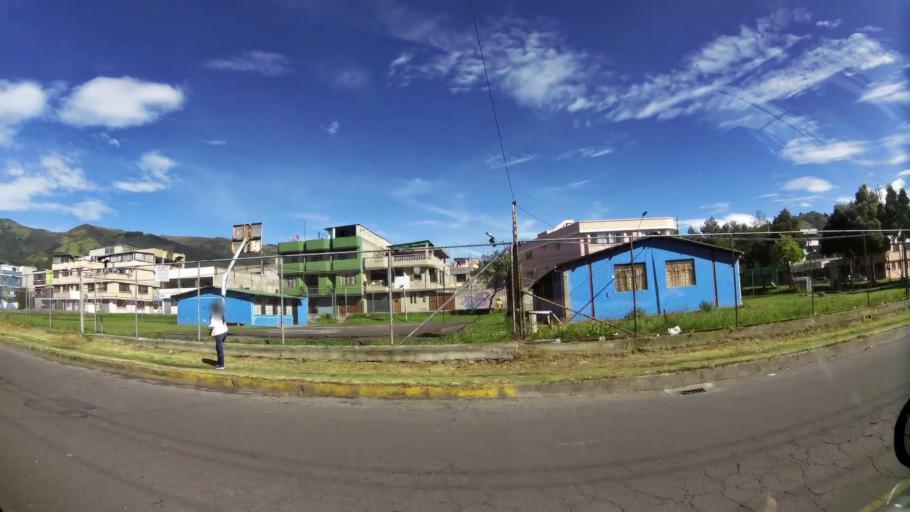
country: EC
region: Pichincha
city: Quito
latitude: -0.2916
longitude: -78.5619
